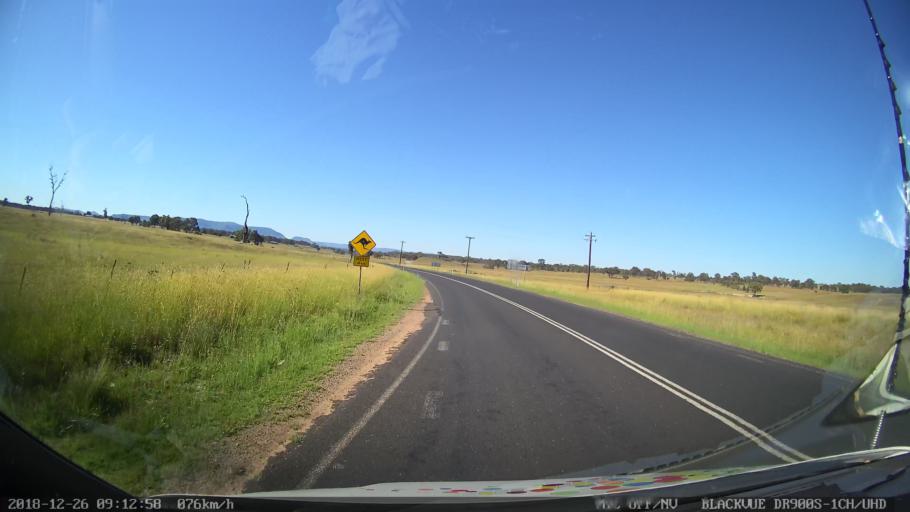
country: AU
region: New South Wales
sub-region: Mid-Western Regional
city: Kandos
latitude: -32.7627
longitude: 149.9786
